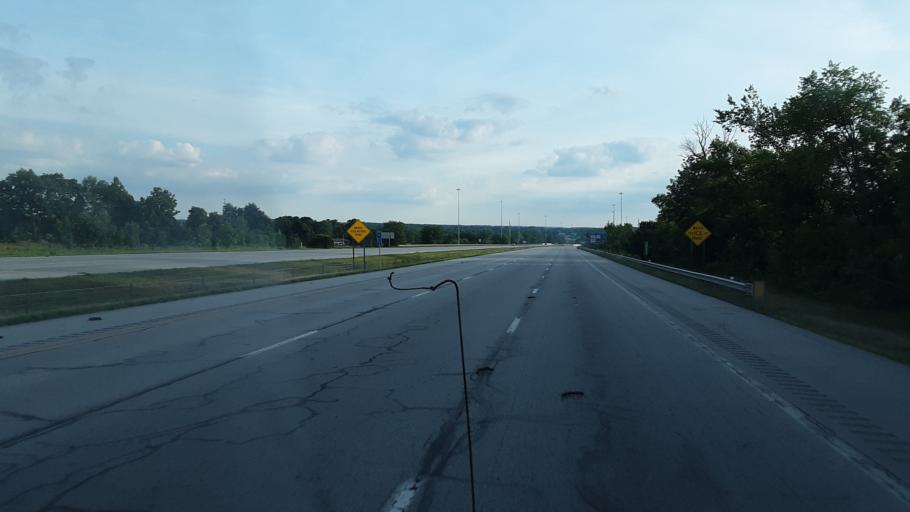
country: US
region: Ohio
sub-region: Medina County
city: Seville
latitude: 41.0425
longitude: -81.8749
